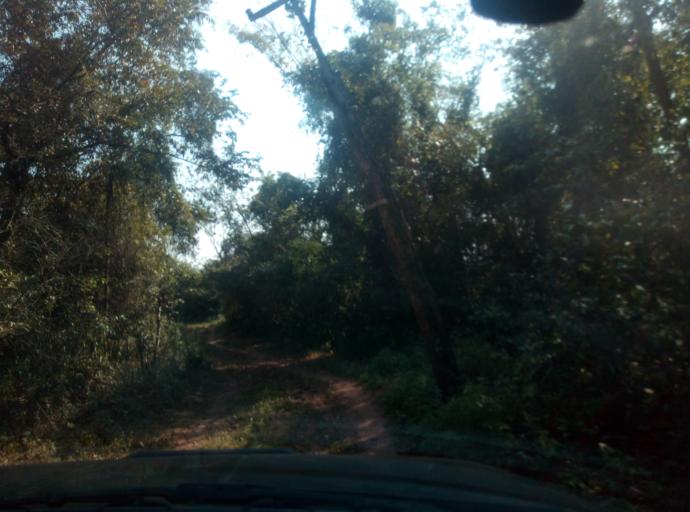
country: PY
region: Caaguazu
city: San Joaquin
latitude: -25.1567
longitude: -56.1257
